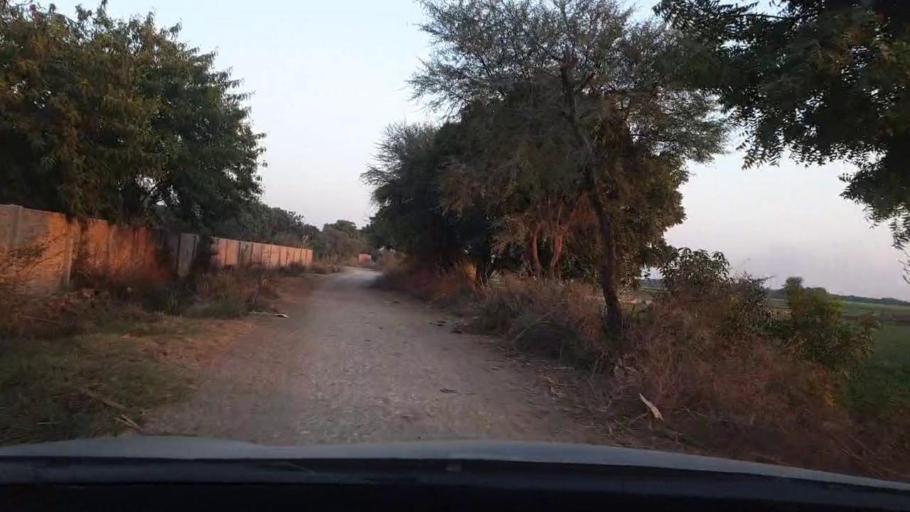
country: PK
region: Sindh
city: Tando Allahyar
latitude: 25.5061
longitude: 68.7421
